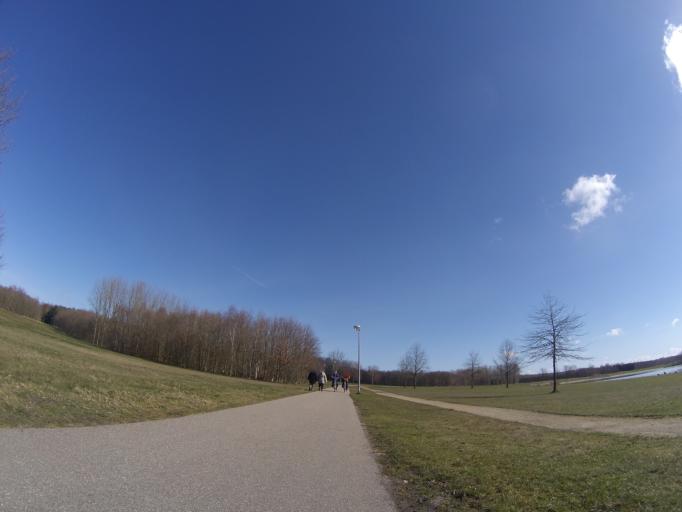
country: NL
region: Drenthe
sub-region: Gemeente Emmen
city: Emmen
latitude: 52.7398
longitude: 6.8985
